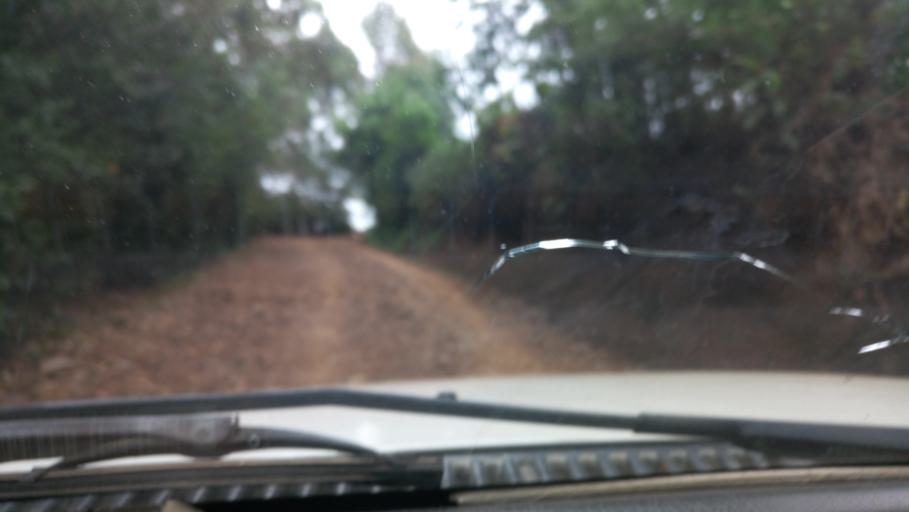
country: KE
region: Murang'a District
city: Kangema
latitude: -0.7921
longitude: 36.9416
